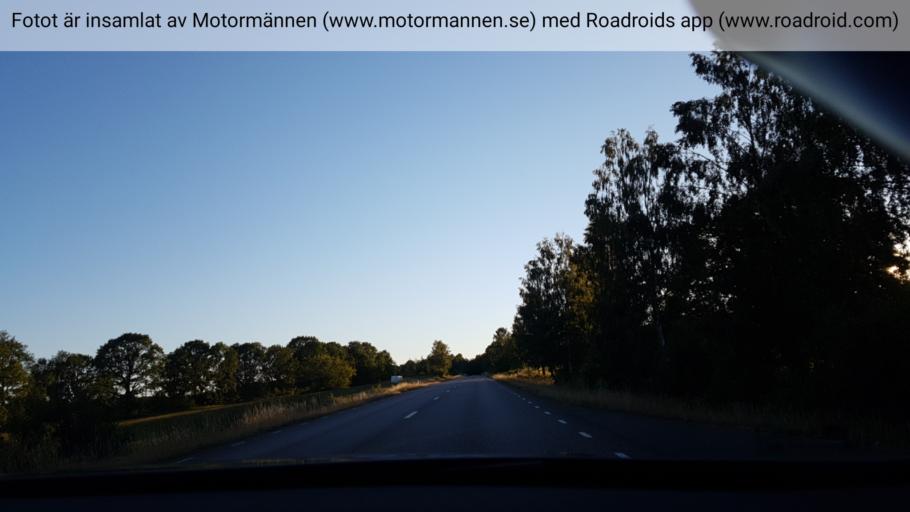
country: SE
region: Vaestra Goetaland
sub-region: Hjo Kommun
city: Hjo
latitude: 58.3219
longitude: 14.2917
